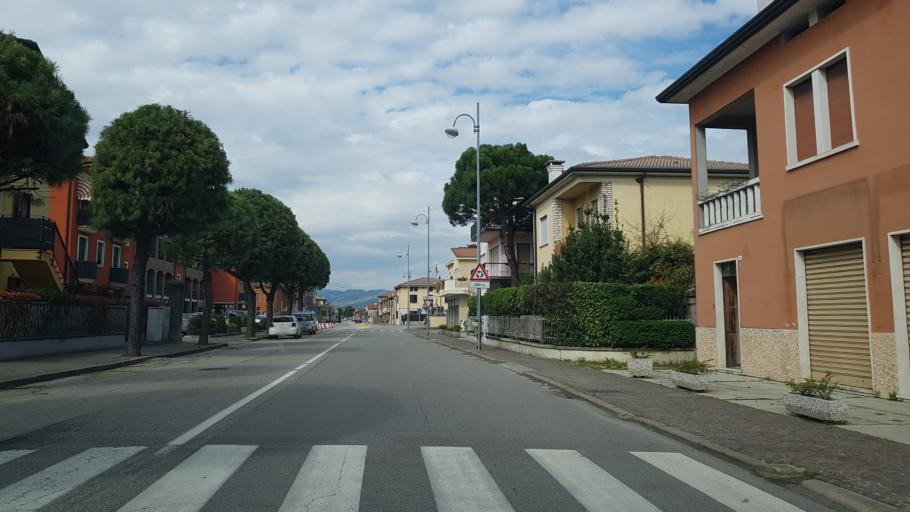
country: IT
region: Veneto
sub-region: Provincia di Verona
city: Belfiore
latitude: 45.3811
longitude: 11.2095
